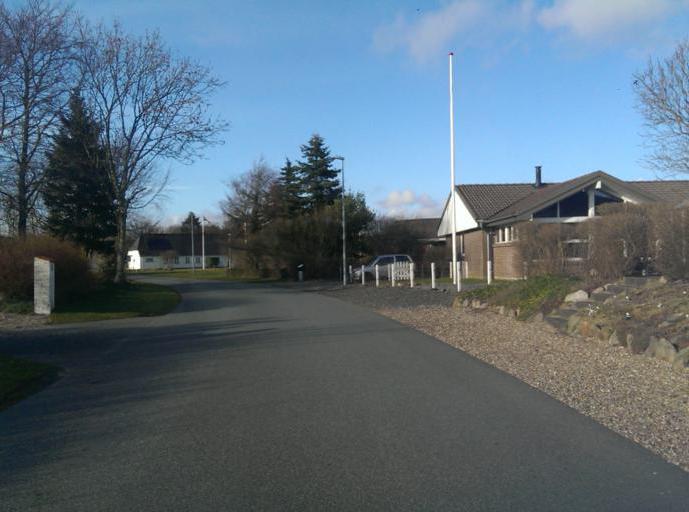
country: DK
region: South Denmark
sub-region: Esbjerg Kommune
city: Bramming
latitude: 55.4320
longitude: 8.6425
